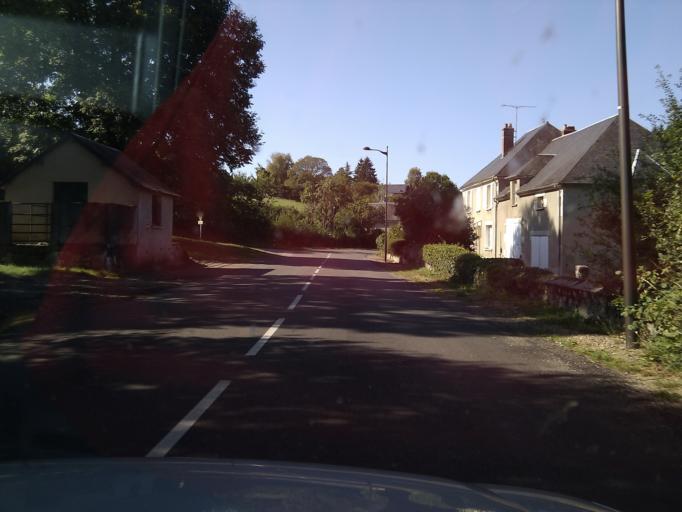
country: FR
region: Bourgogne
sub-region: Departement de la Nievre
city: Lormes
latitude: 47.2842
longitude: 4.0118
